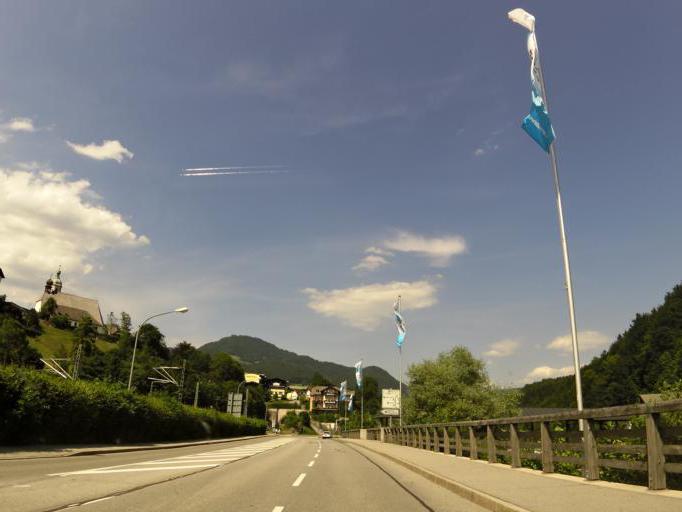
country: DE
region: Bavaria
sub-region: Upper Bavaria
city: Berchtesgaden
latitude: 47.6273
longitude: 13.0014
